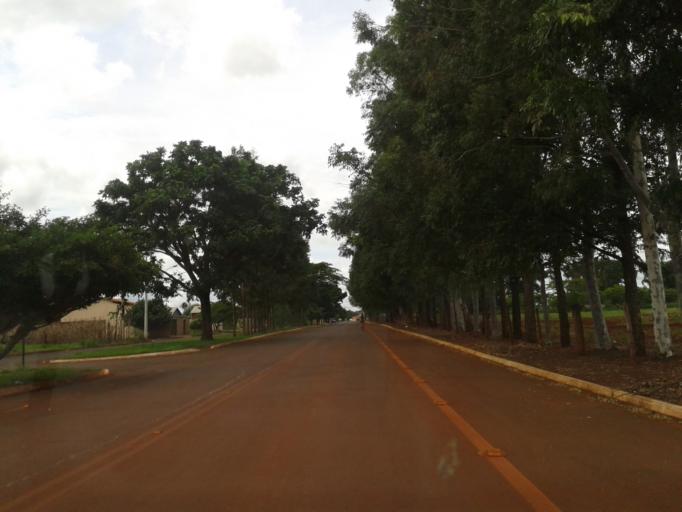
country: BR
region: Minas Gerais
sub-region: Centralina
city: Centralina
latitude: -18.5898
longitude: -49.2053
